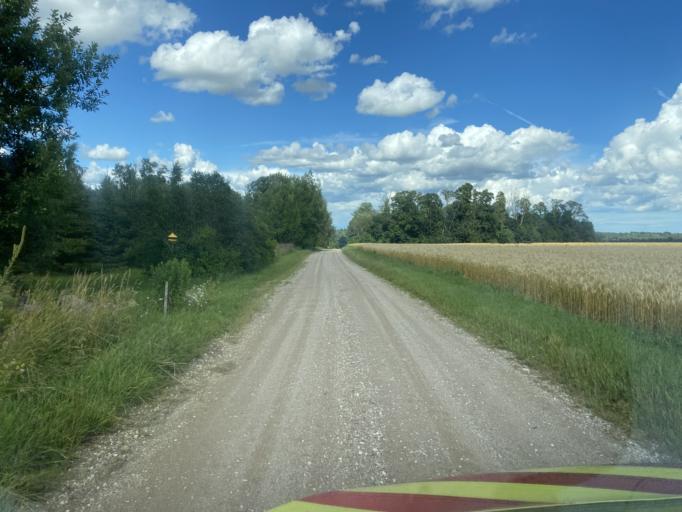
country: EE
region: Viljandimaa
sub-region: Viiratsi vald
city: Viiratsi
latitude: 58.2944
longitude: 25.6098
